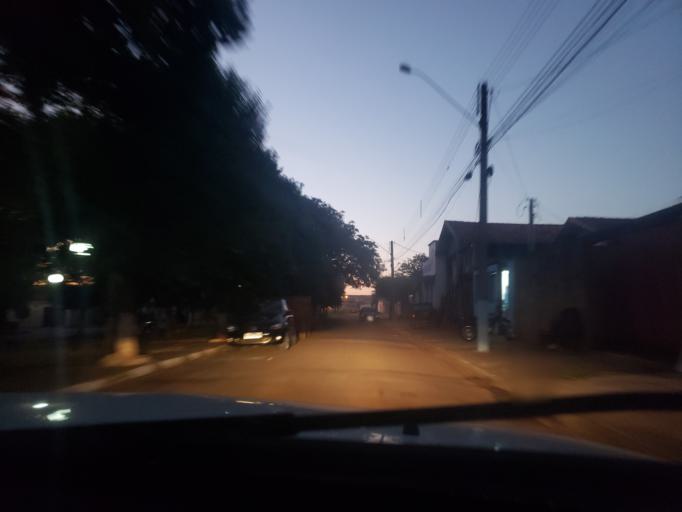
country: BR
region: Sao Paulo
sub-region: Conchal
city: Conchal
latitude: -22.2917
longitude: -47.1319
